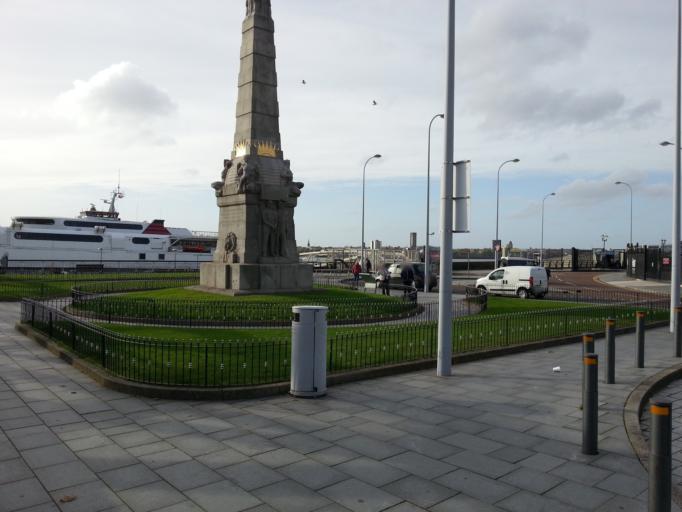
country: GB
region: England
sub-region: Liverpool
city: Liverpool
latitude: 53.4061
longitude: -2.9978
